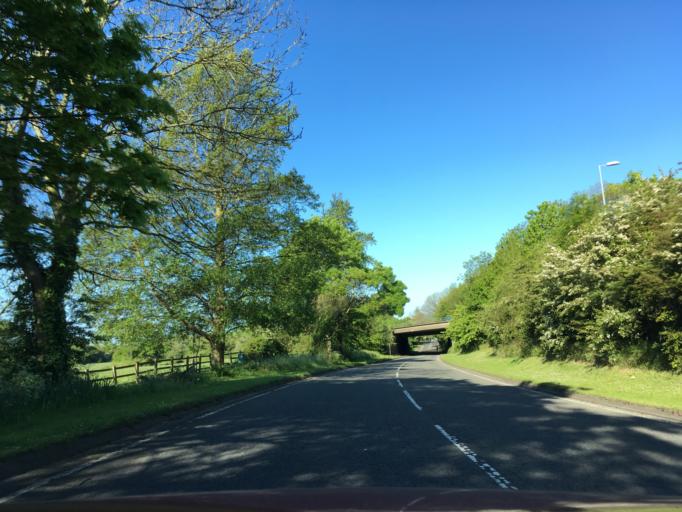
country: GB
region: England
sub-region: North Somerset
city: Clevedon
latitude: 51.4398
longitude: -2.8258
